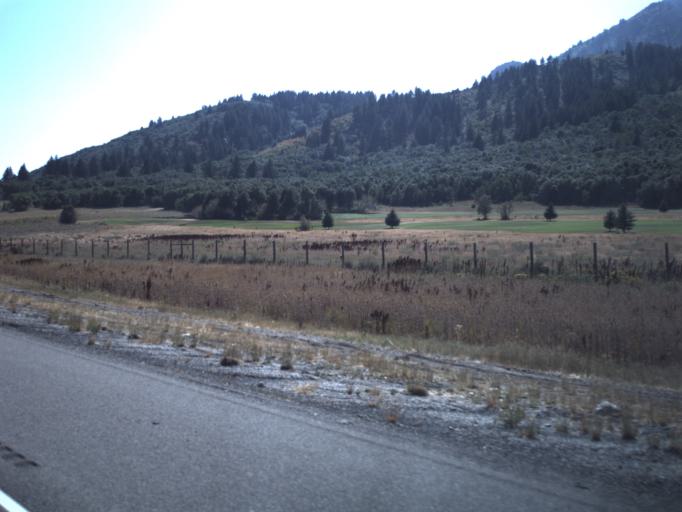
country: US
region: Utah
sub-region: Cache County
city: Wellsville
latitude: 41.5832
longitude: -111.9750
